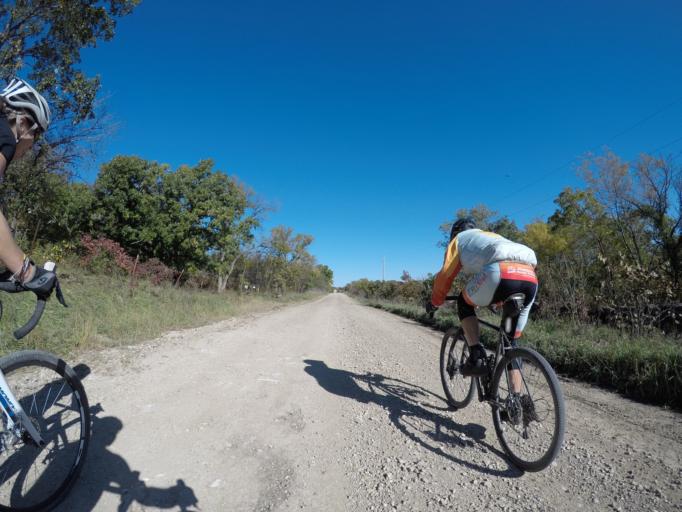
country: US
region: Kansas
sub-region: Wabaunsee County
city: Alma
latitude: 38.9019
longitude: -96.3630
